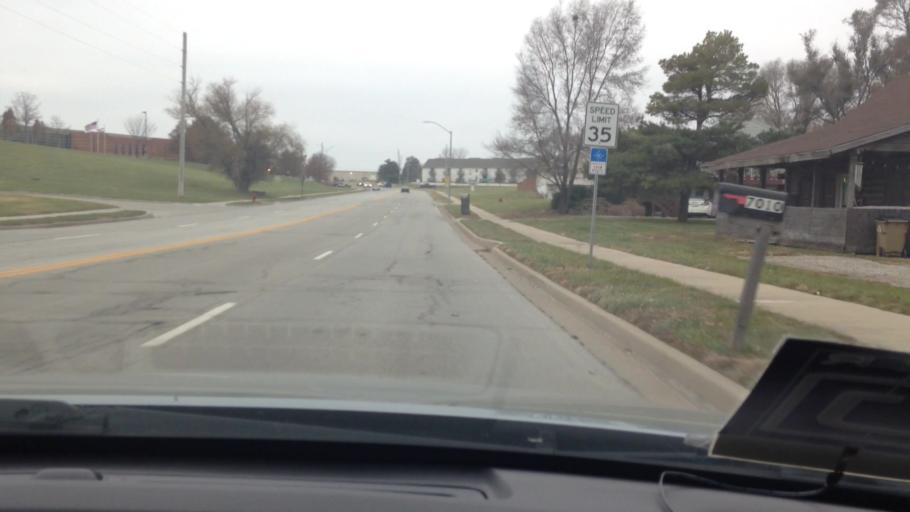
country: US
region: Missouri
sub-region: Cass County
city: Belton
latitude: 38.8281
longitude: -94.5123
